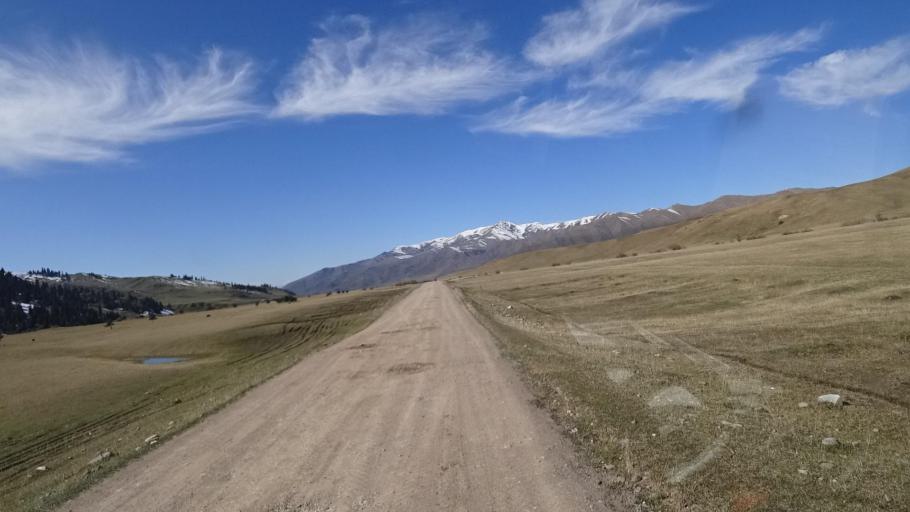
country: KZ
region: Almaty Oblysy
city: Kegen
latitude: 42.7292
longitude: 79.0427
